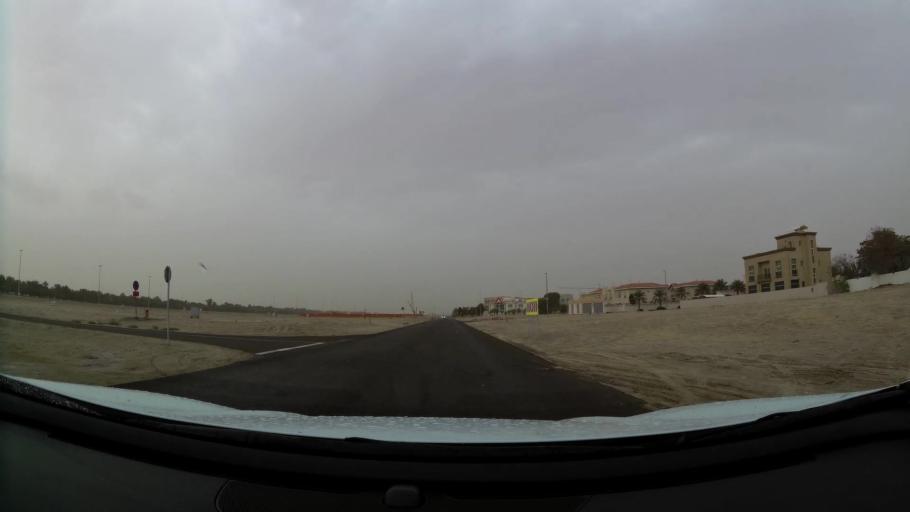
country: AE
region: Abu Dhabi
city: Abu Dhabi
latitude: 24.4058
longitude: 54.5994
